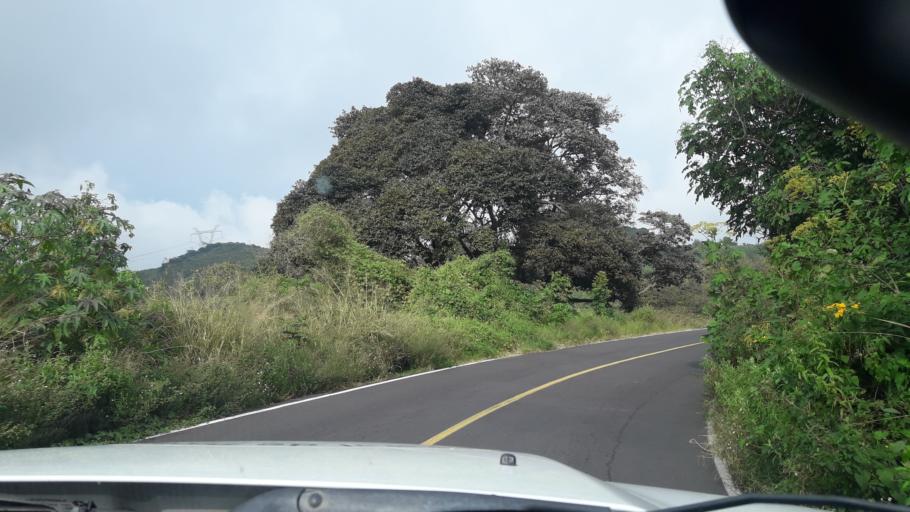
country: MX
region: Colima
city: Queseria
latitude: 19.4093
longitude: -103.6359
